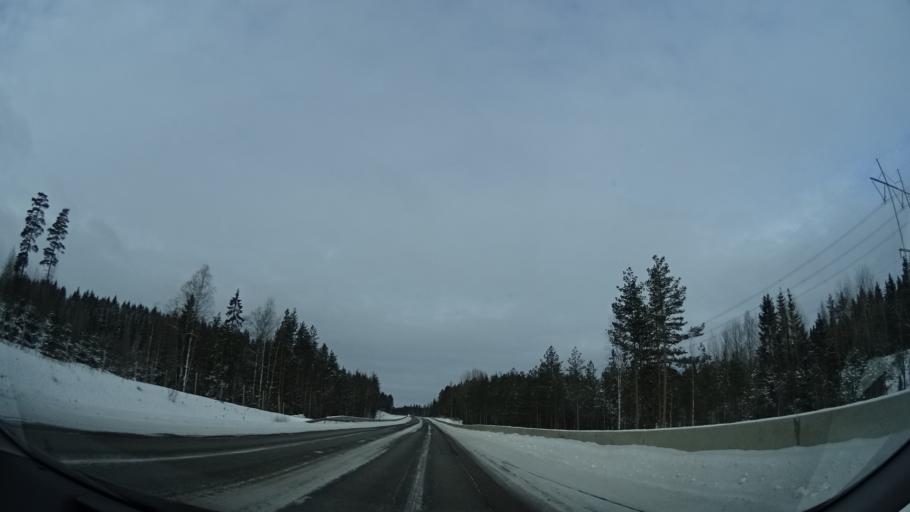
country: FI
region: Uusimaa
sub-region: Helsinki
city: Kaerkoelae
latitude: 60.6023
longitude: 24.0802
